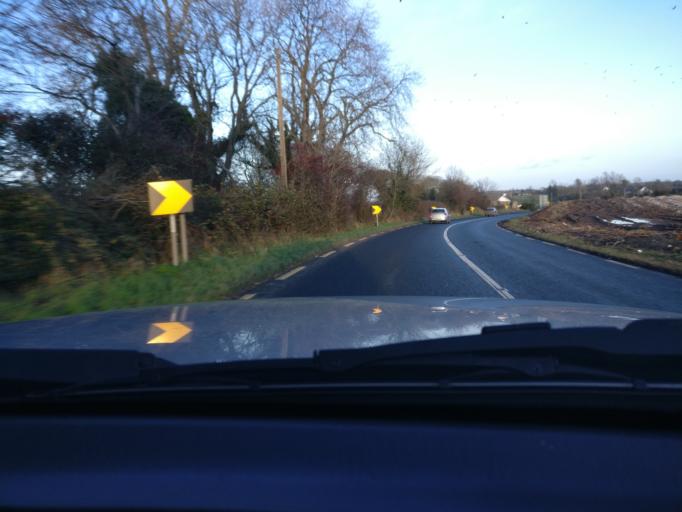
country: IE
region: Leinster
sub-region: Lu
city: Ardee
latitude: 53.8477
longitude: -6.5988
